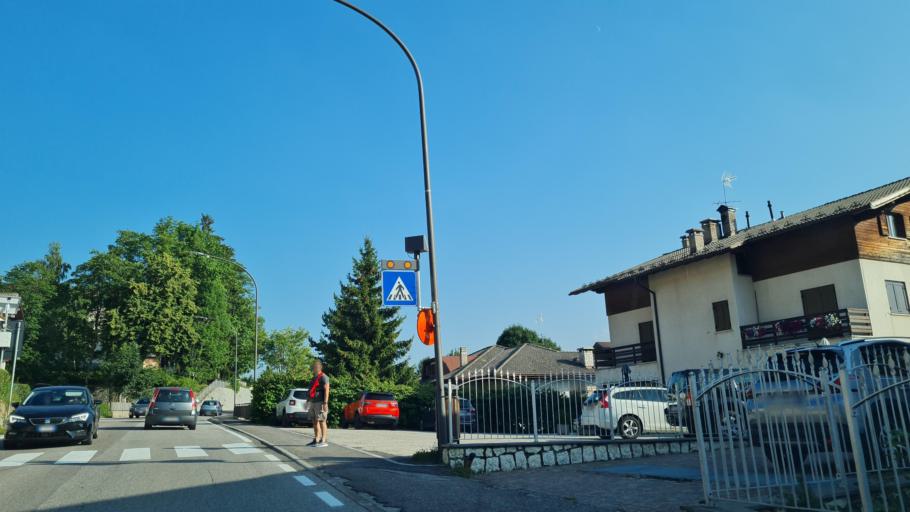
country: IT
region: Trentino-Alto Adige
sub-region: Provincia di Trento
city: Gionghi-Cappella
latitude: 45.9407
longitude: 11.2722
